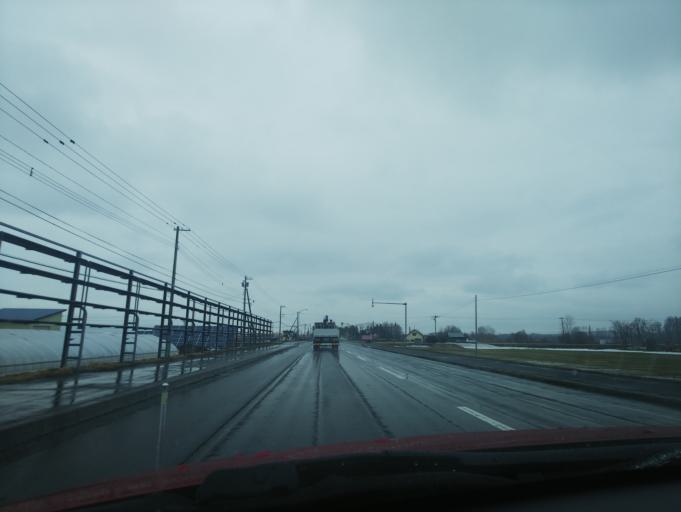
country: JP
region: Hokkaido
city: Nayoro
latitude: 44.2143
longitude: 142.3949
